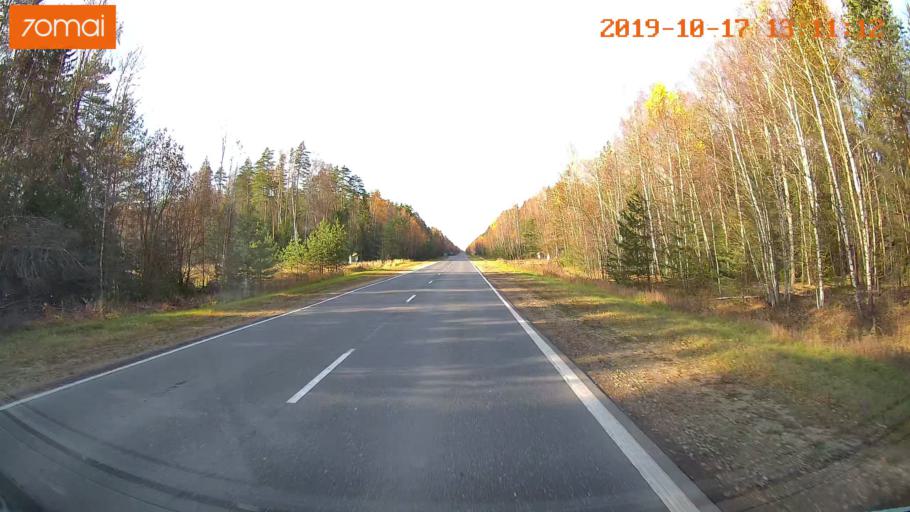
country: RU
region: Rjazan
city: Syntul
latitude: 55.0256
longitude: 41.2405
